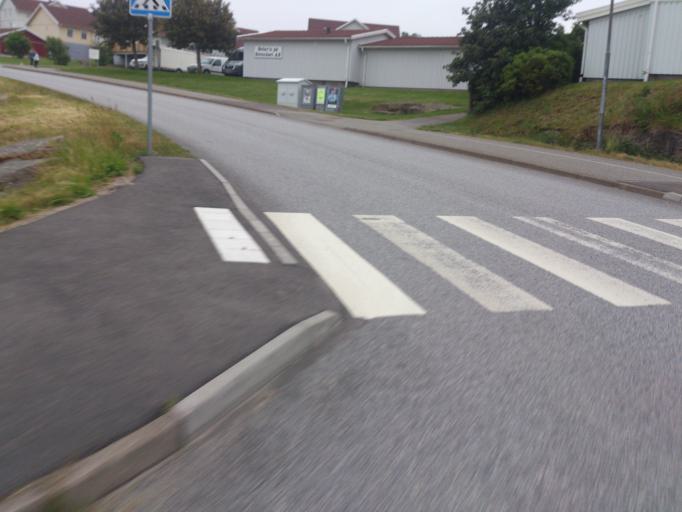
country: SE
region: Vaestra Goetaland
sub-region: Sotenas Kommun
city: Kungshamn
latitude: 58.3793
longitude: 11.2630
